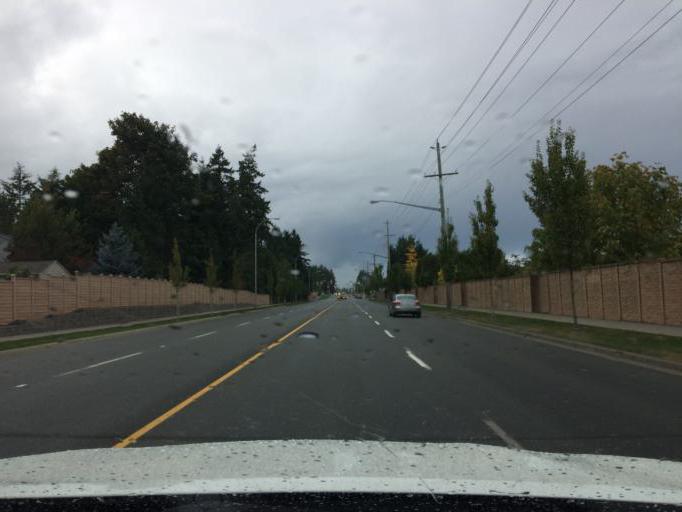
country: CA
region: British Columbia
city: Courtenay
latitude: 49.7068
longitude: -124.9611
